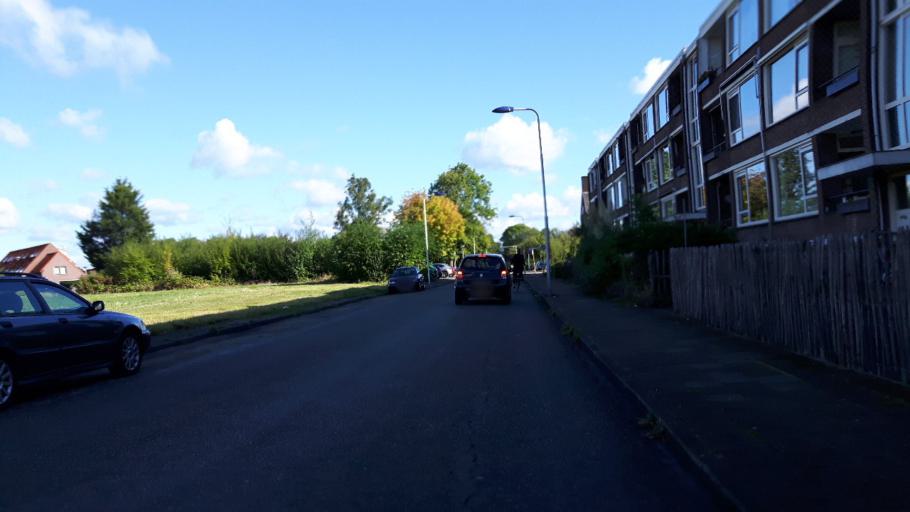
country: NL
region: Gelderland
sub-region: Gemeente Culemborg
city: Culemborg
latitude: 51.9502
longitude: 5.2185
